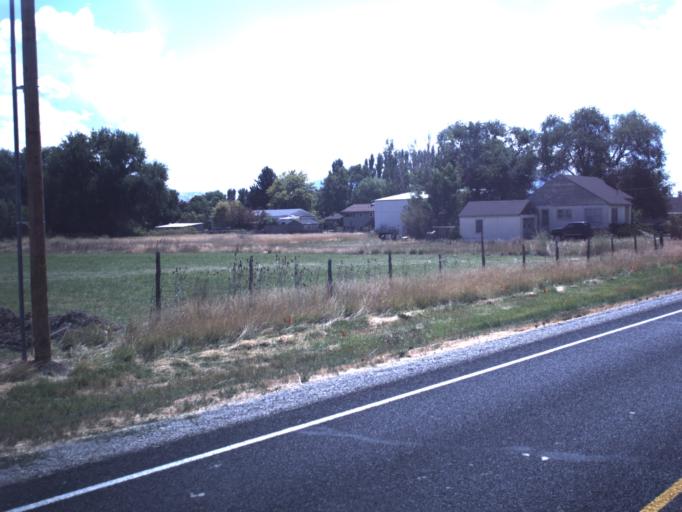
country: US
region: Utah
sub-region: Box Elder County
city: Honeyville
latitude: 41.6223
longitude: -112.1269
